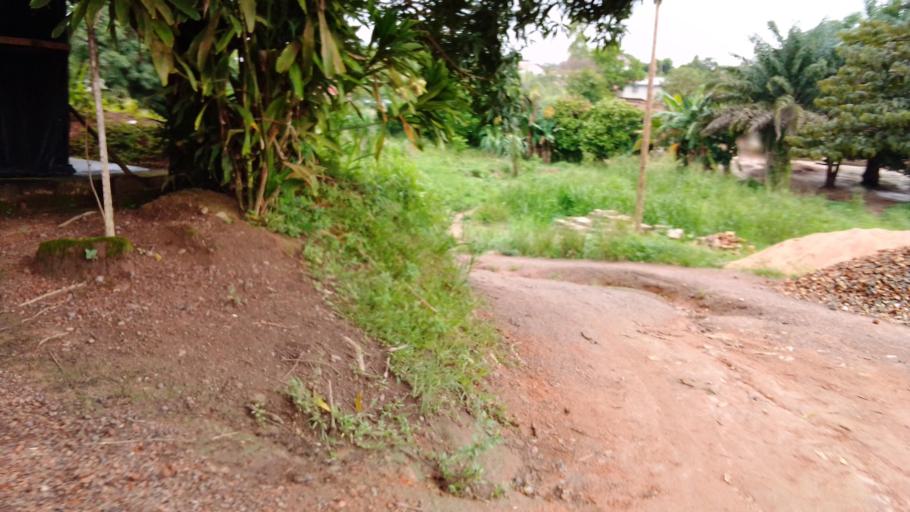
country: SL
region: Eastern Province
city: Kenema
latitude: 7.8785
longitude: -11.1640
